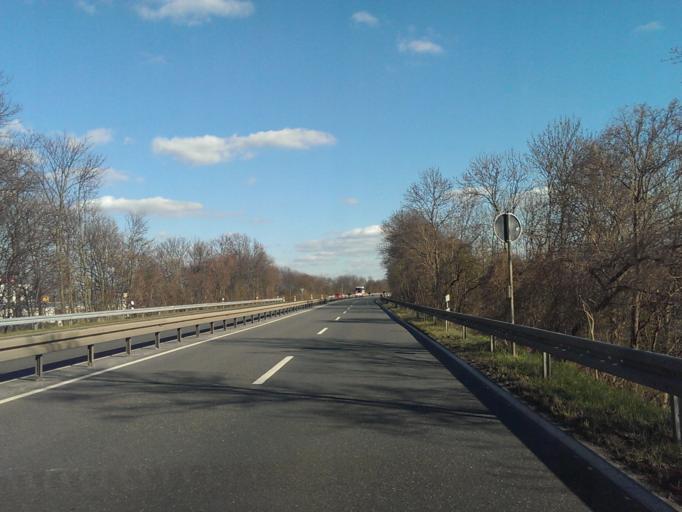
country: DE
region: Lower Saxony
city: Hildesheim
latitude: 52.1640
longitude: 9.9647
